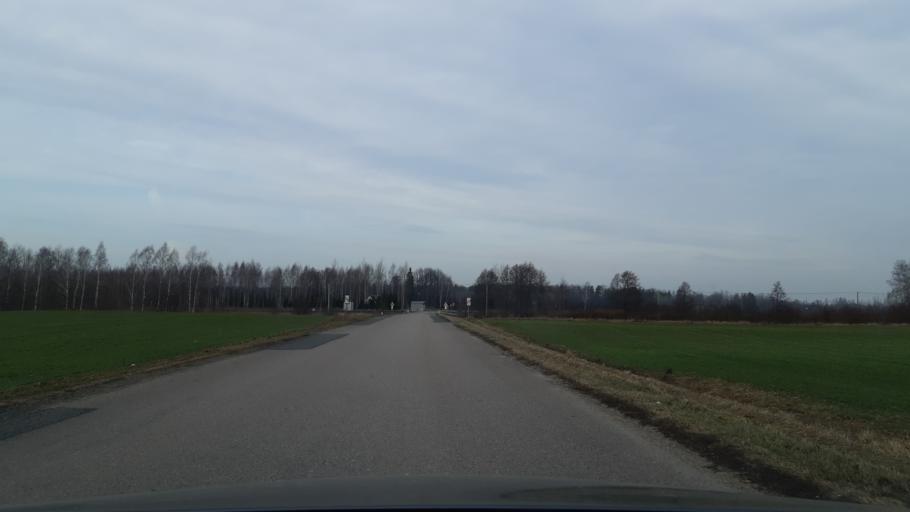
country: LT
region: Marijampoles apskritis
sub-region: Marijampole Municipality
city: Marijampole
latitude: 54.7251
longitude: 23.3367
